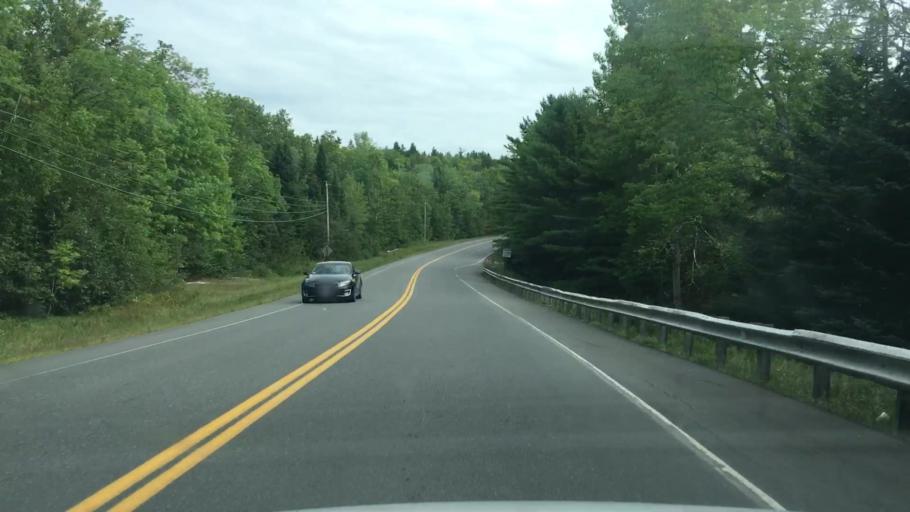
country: US
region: Maine
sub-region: Piscataquis County
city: Dover-Foxcroft
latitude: 45.2129
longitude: -69.1701
